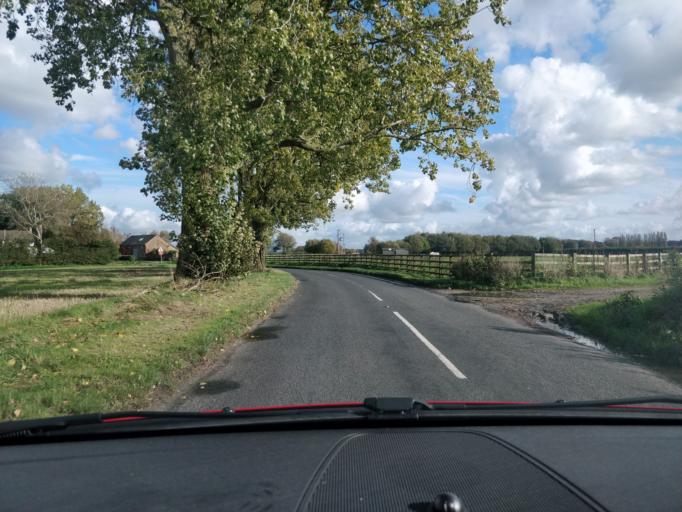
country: GB
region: England
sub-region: Lancashire
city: Ormskirk
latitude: 53.5857
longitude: -2.8353
